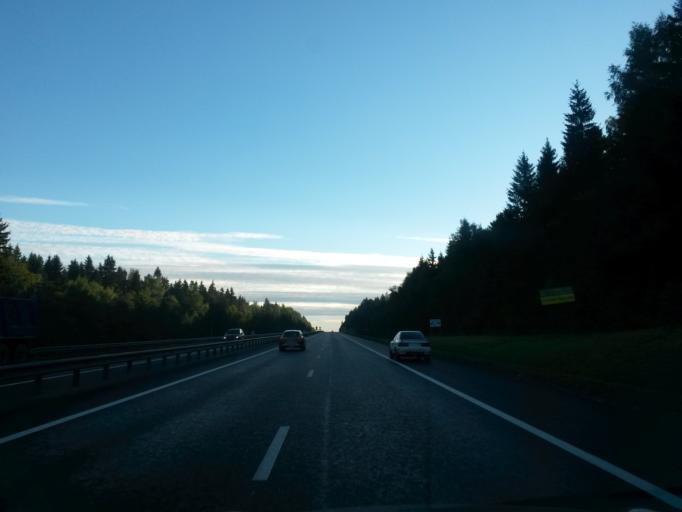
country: RU
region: Moskovskaya
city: Svatkovo
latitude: 56.3636
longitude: 38.2952
